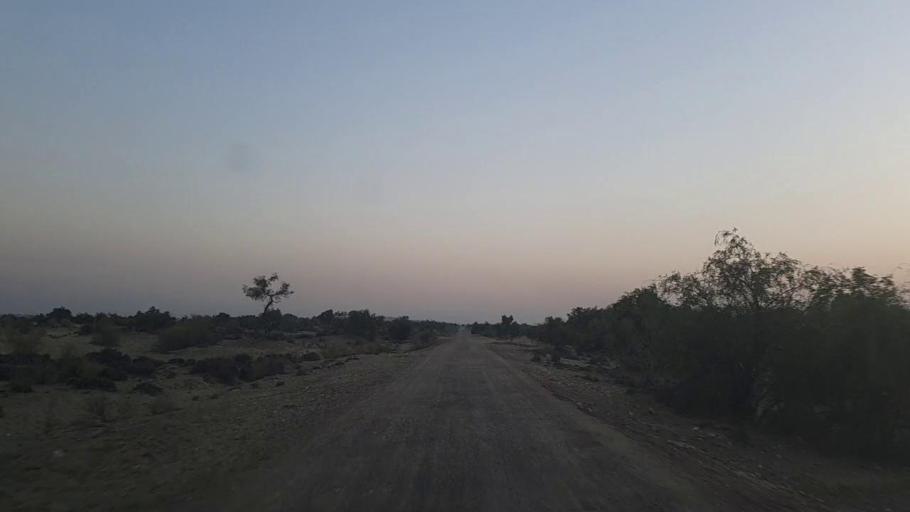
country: PK
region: Sindh
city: Jam Sahib
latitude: 26.4139
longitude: 68.8094
